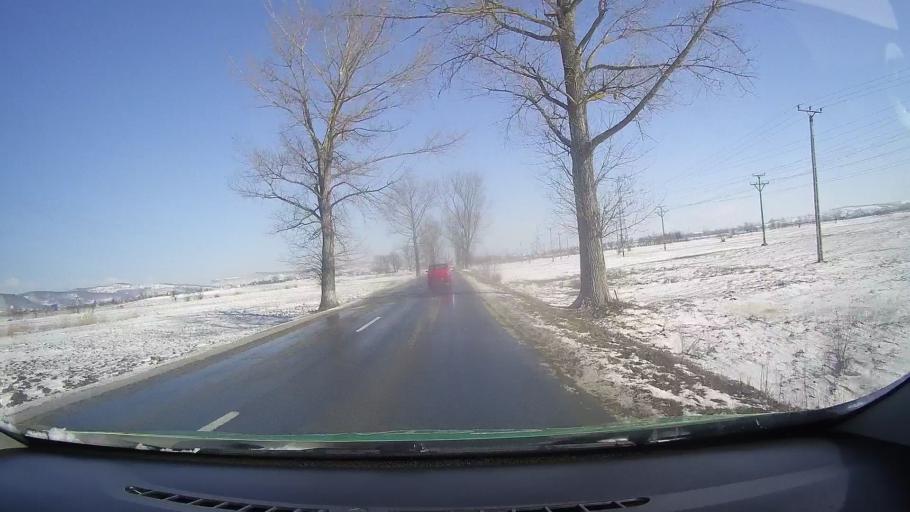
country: RO
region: Sibiu
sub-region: Comuna Avrig
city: Marsa
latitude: 45.7128
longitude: 24.3698
